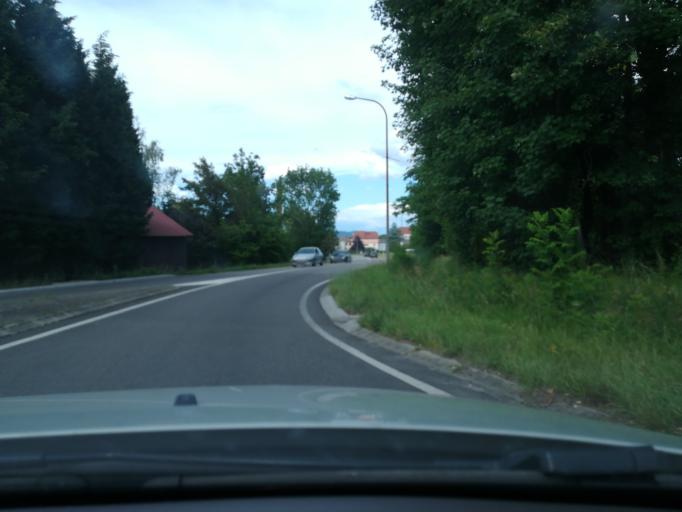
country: FR
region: Alsace
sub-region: Departement du Bas-Rhin
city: Ingwiller
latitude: 48.8634
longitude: 7.4704
